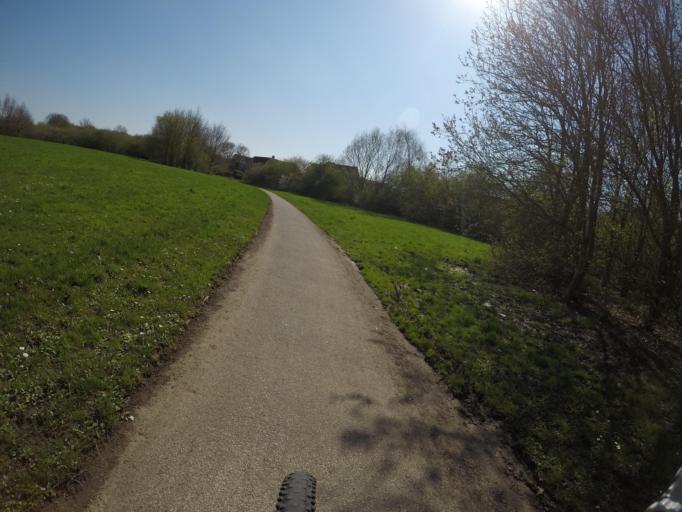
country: GB
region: England
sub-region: City of York
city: York
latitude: 53.9820
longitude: -1.0936
